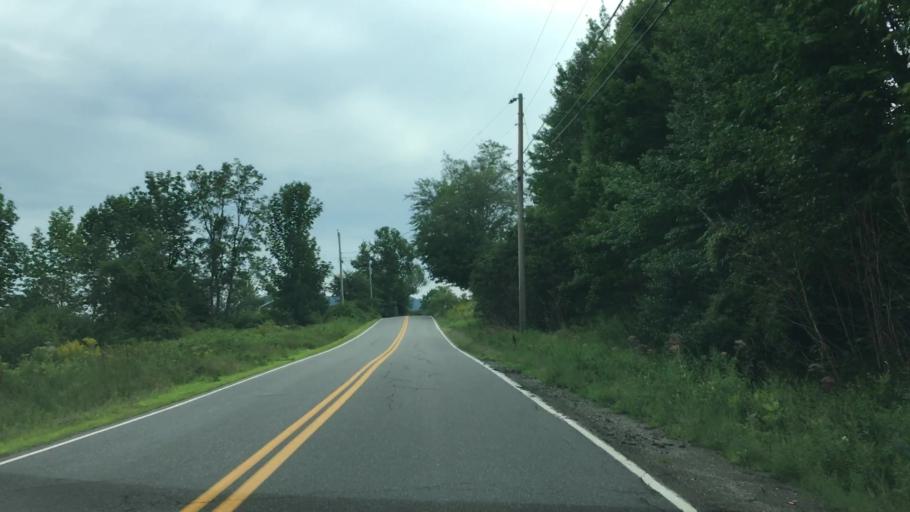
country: US
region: Maine
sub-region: Knox County
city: Hope
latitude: 44.3040
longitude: -69.1044
